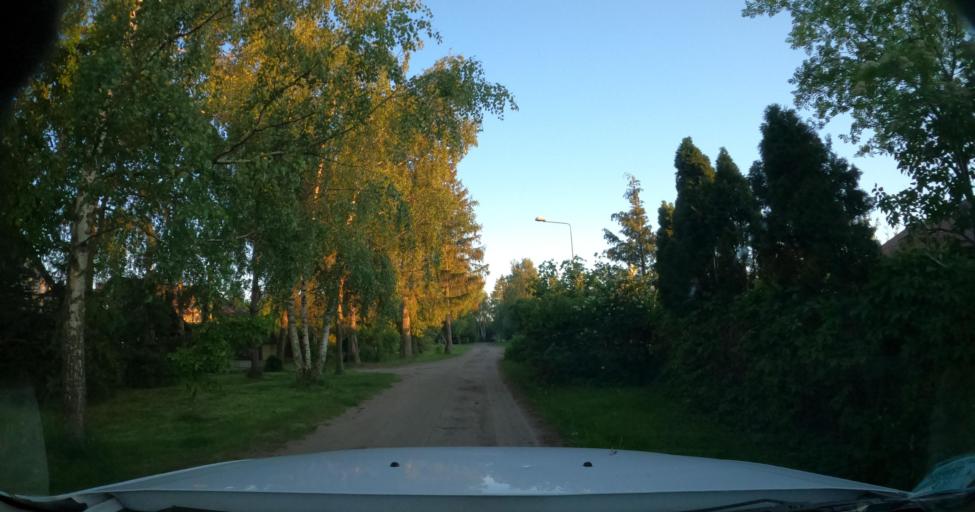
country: PL
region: Pomeranian Voivodeship
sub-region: Slupsk
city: Slupsk
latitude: 54.4728
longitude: 16.9990
